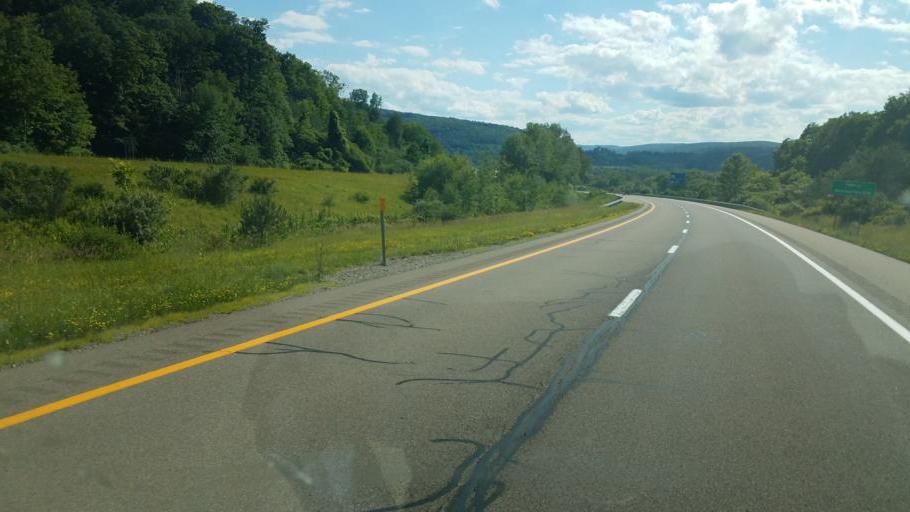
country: US
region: New York
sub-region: Steuben County
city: Hornell
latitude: 42.3791
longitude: -77.6664
